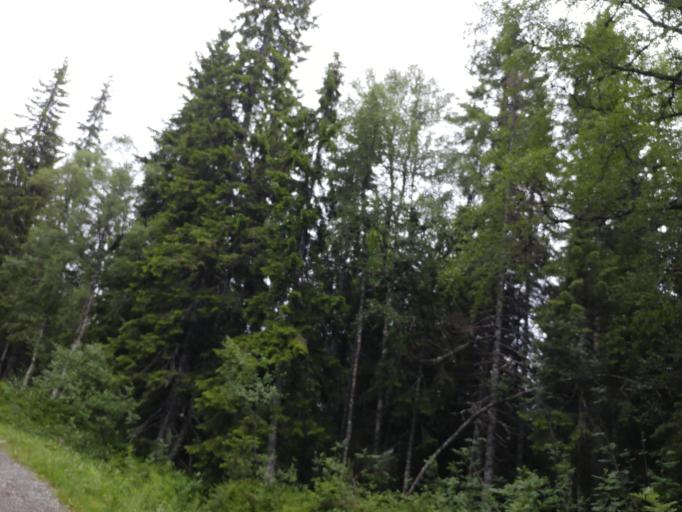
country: NO
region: Sor-Trondelag
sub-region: Melhus
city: Melhus
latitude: 63.4000
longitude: 10.2624
